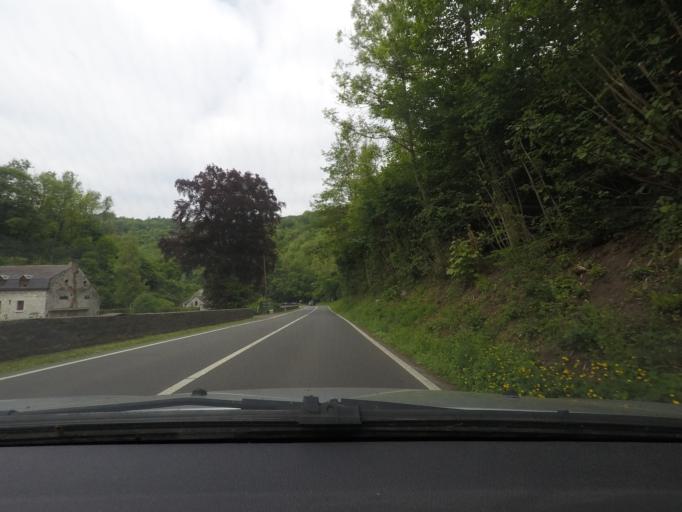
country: BE
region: Wallonia
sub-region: Province de Namur
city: Gesves
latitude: 50.4494
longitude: 5.0109
